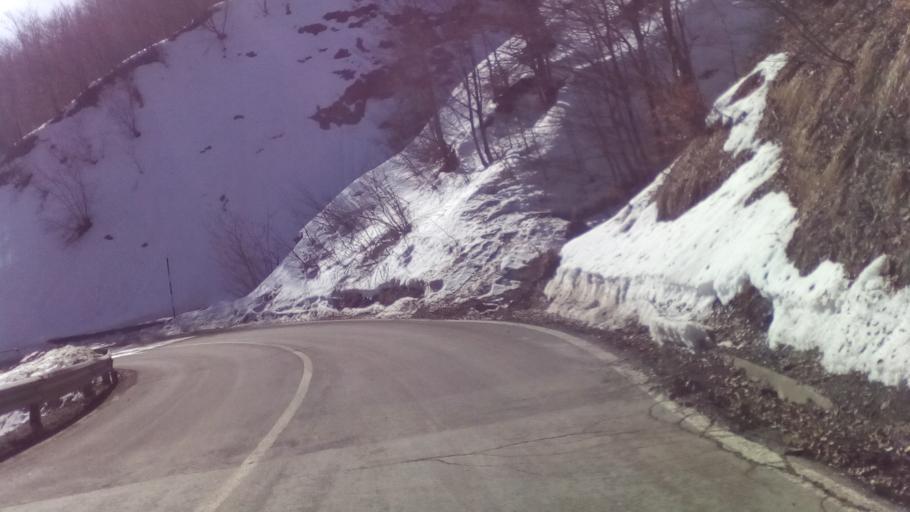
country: IT
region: Tuscany
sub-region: Provincia di Lucca
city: Castiglione di Garfagnana
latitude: 44.2067
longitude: 10.4899
